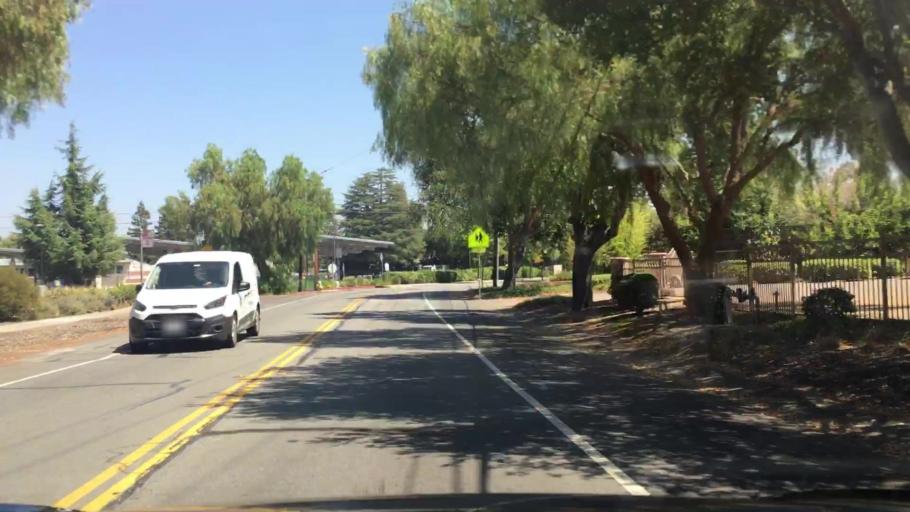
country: US
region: California
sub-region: Santa Clara County
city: Los Altos
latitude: 37.3711
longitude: -122.1089
